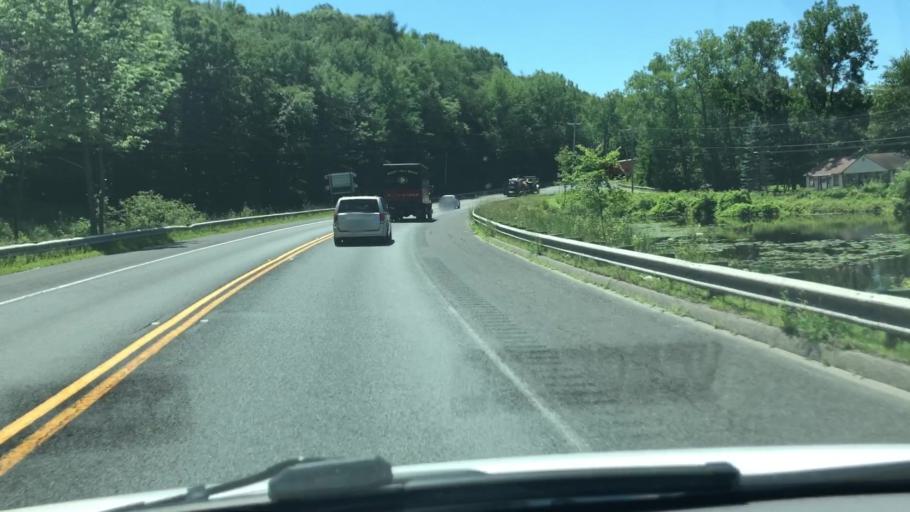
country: US
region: Massachusetts
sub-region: Berkshire County
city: Lanesborough
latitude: 42.5483
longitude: -73.1655
